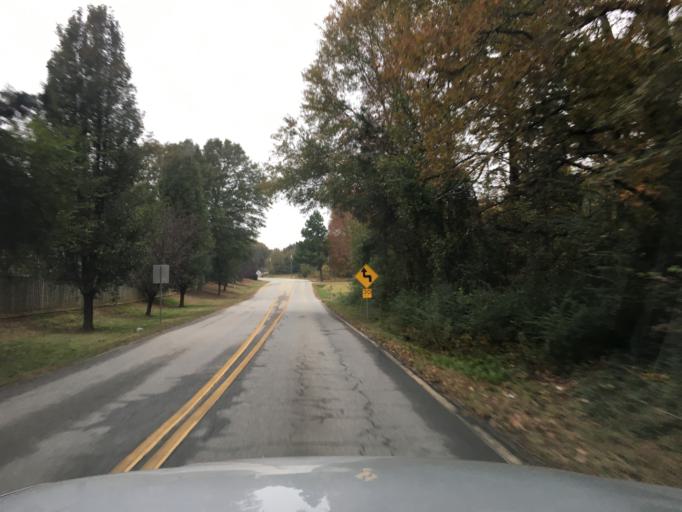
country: US
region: South Carolina
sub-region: Greenville County
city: Five Forks
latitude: 34.8251
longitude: -82.2695
